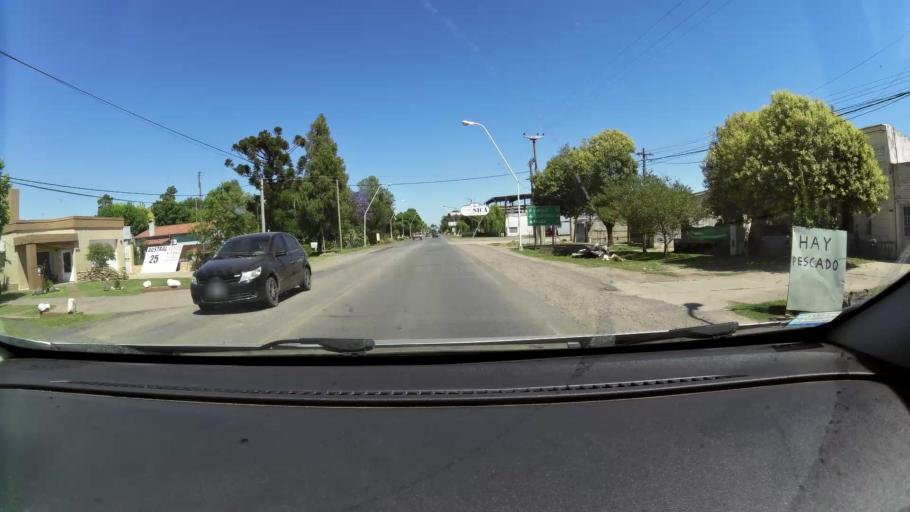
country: AR
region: Santa Fe
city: Esperanza
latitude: -31.4380
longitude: -60.9491
